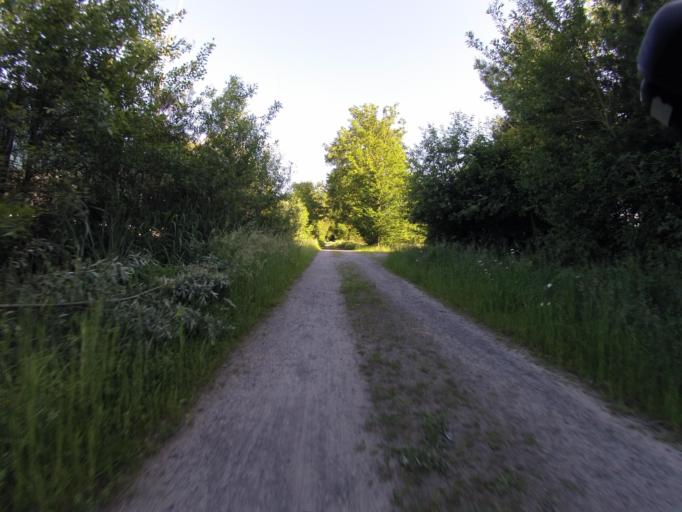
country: DE
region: Lower Saxony
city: Bad Bentheim
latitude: 52.3123
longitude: 7.1345
